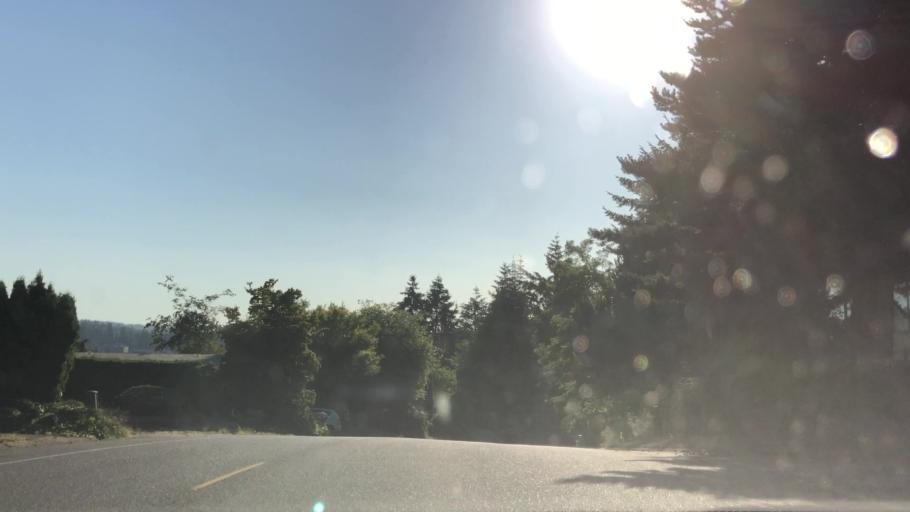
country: US
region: Washington
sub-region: King County
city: Woodinville
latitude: 47.7654
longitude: -122.1714
